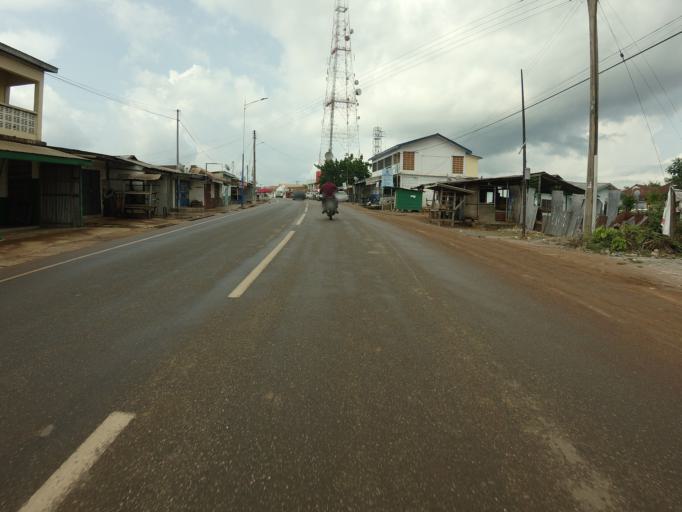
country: GH
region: Volta
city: Hohoe
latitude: 7.1518
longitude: 0.4744
